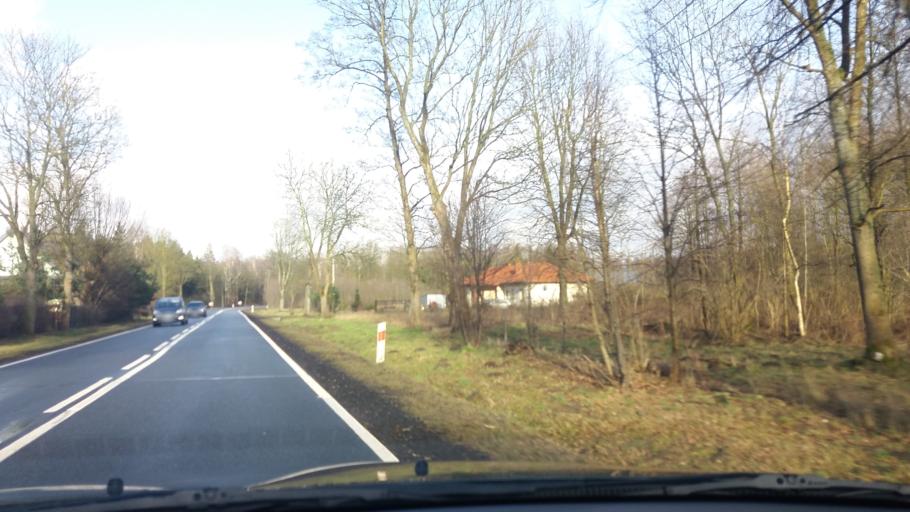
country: PL
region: Masovian Voivodeship
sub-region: Powiat przasnyski
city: Chorzele
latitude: 53.2834
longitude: 20.9015
